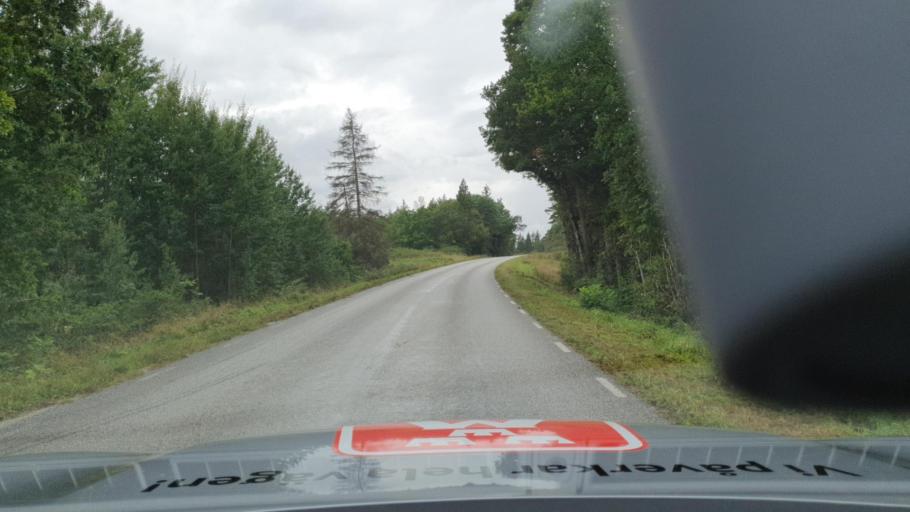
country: SE
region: Gotland
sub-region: Gotland
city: Slite
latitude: 57.5917
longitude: 18.6173
